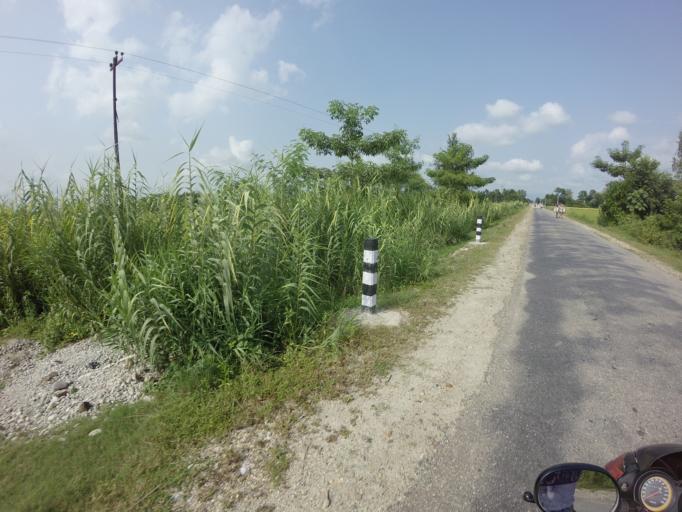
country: NP
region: Far Western
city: Tikapur
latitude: 28.4799
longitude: 81.0785
